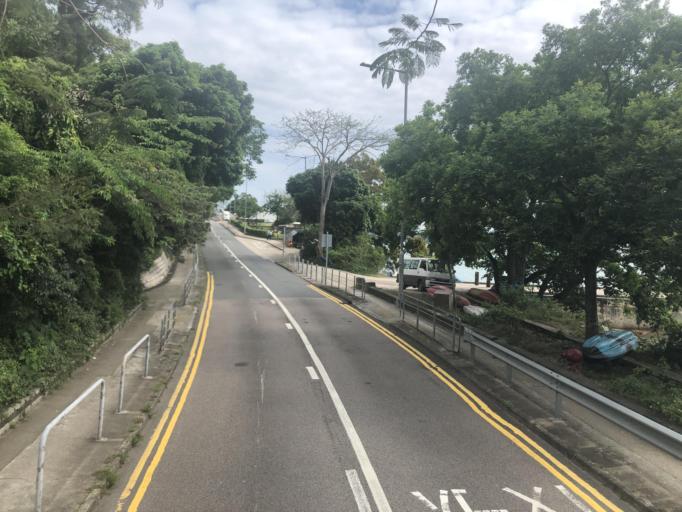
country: HK
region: Sai Kung
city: Sai Kung
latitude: 22.3931
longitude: 114.2892
